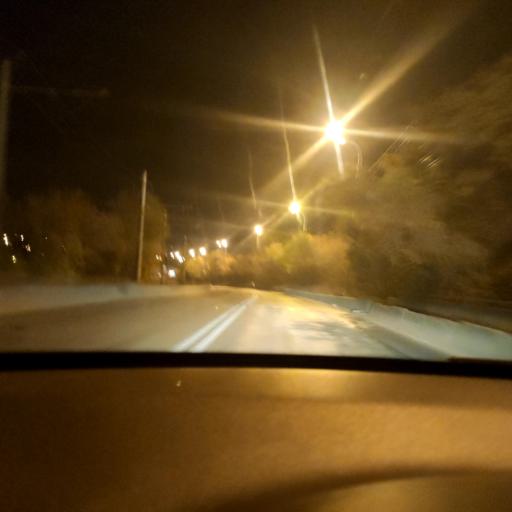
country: RU
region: Samara
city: Smyshlyayevka
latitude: 53.2216
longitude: 50.2896
